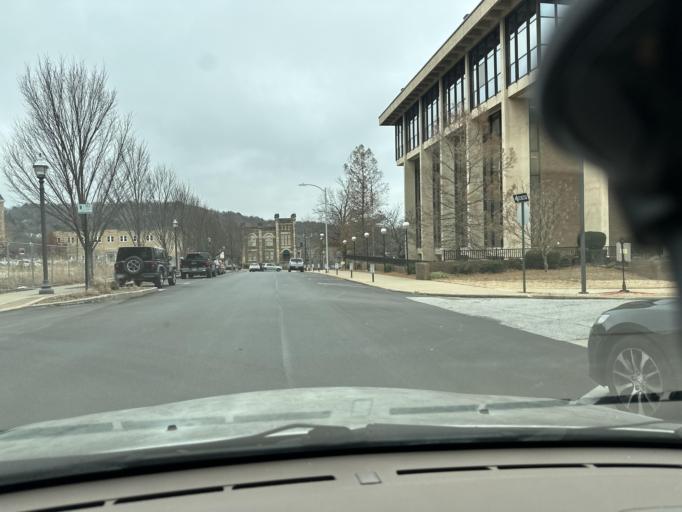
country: US
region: Arkansas
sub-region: Washington County
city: Fayetteville
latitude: 36.0619
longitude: -94.1592
